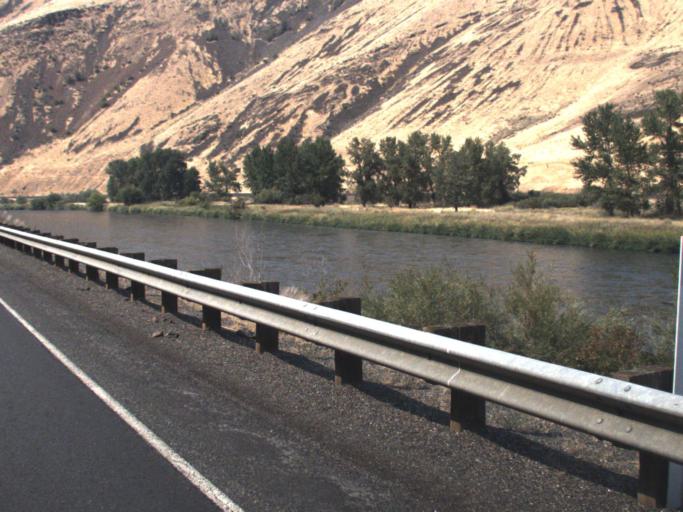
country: US
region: Washington
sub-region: Yakima County
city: Selah
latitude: 46.8016
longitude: -120.4546
